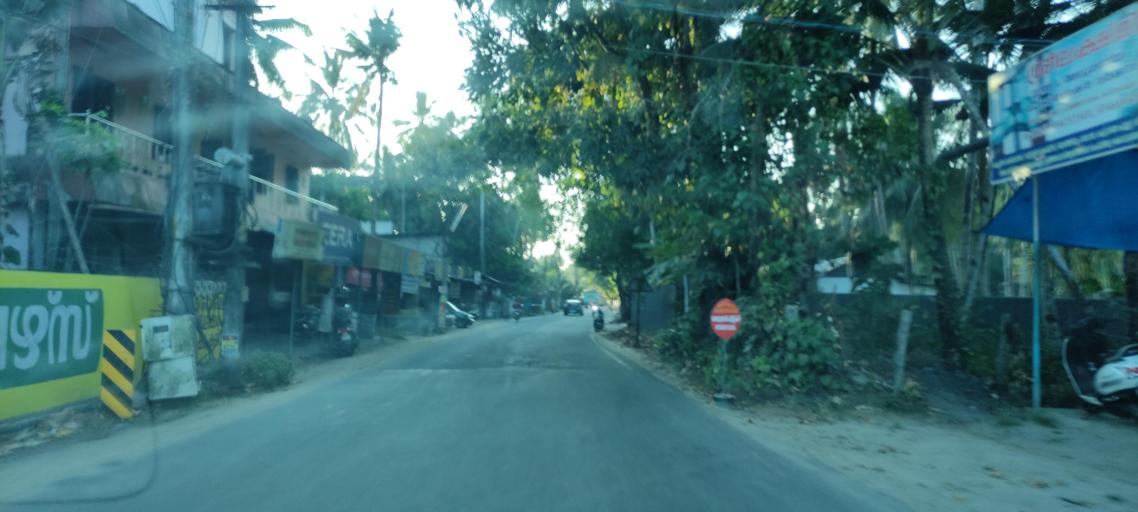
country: IN
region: Kerala
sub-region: Alappuzha
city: Kayankulam
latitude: 9.1770
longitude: 76.4837
